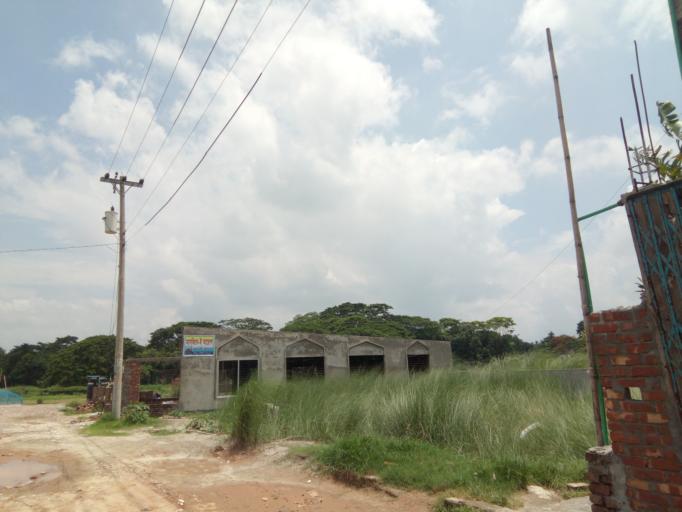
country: BD
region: Dhaka
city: Azimpur
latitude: 23.7335
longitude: 90.3412
